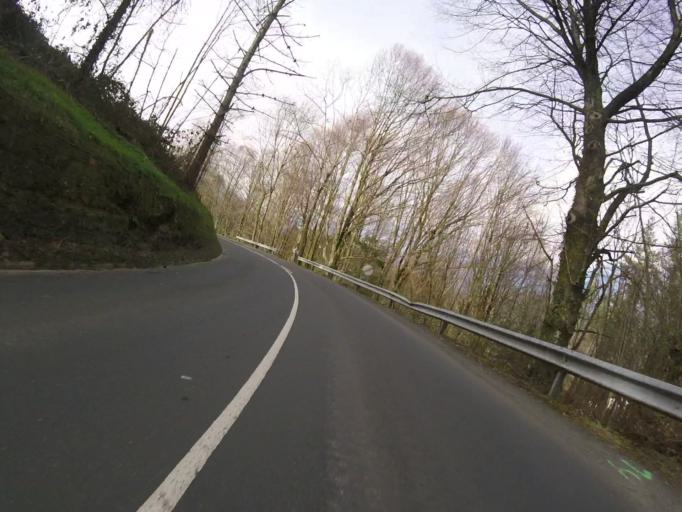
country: ES
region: Basque Country
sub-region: Provincia de Guipuzcoa
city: Beizama
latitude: 43.1655
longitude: -2.2189
